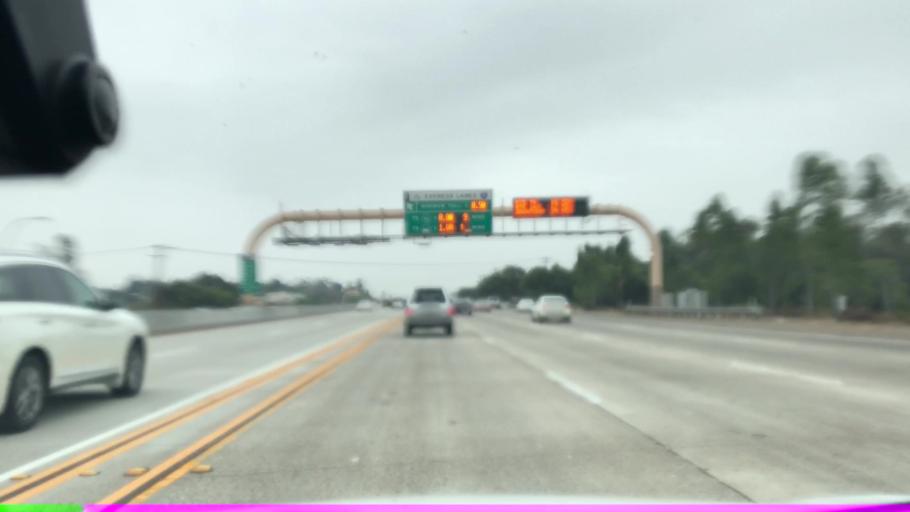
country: US
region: California
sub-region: San Diego County
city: Escondido
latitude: 33.0949
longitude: -117.0854
